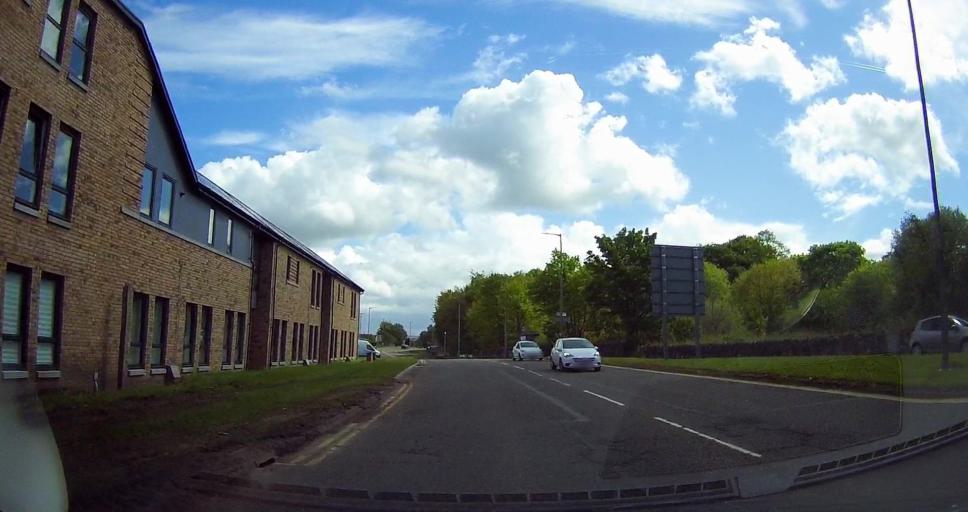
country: GB
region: Scotland
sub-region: Falkirk
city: Larbert
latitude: 56.0300
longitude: -3.8444
